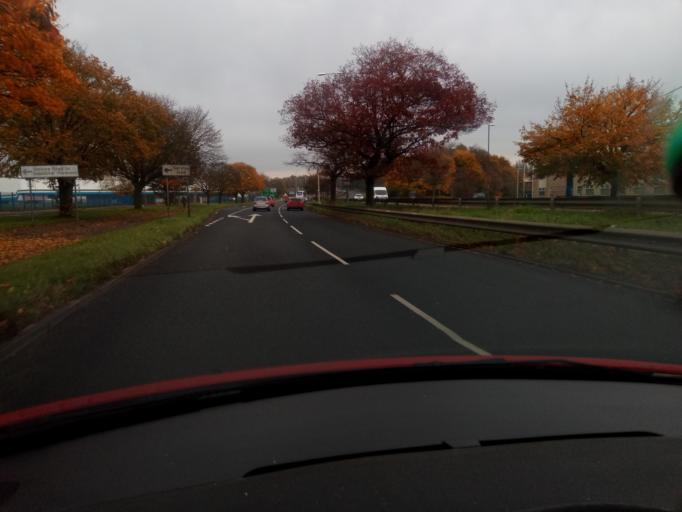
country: GB
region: England
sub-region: Derbyshire
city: Borrowash
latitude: 52.9119
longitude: -1.4278
